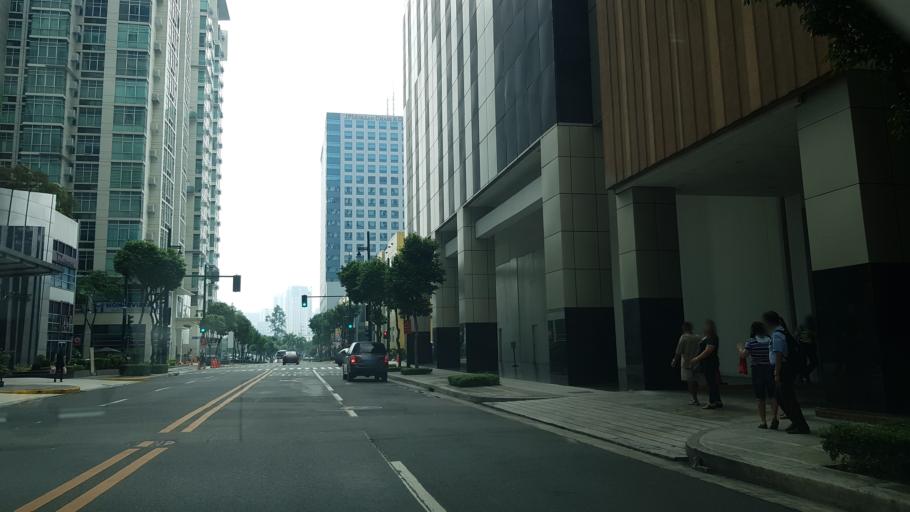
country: PH
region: Metro Manila
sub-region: Makati City
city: Makati City
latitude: 14.5542
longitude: 121.0457
